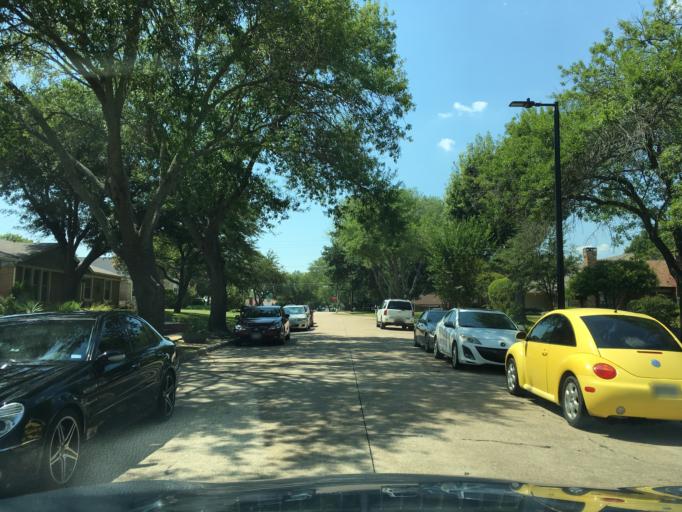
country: US
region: Texas
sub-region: Collin County
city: Plano
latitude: 32.9674
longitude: -96.6690
